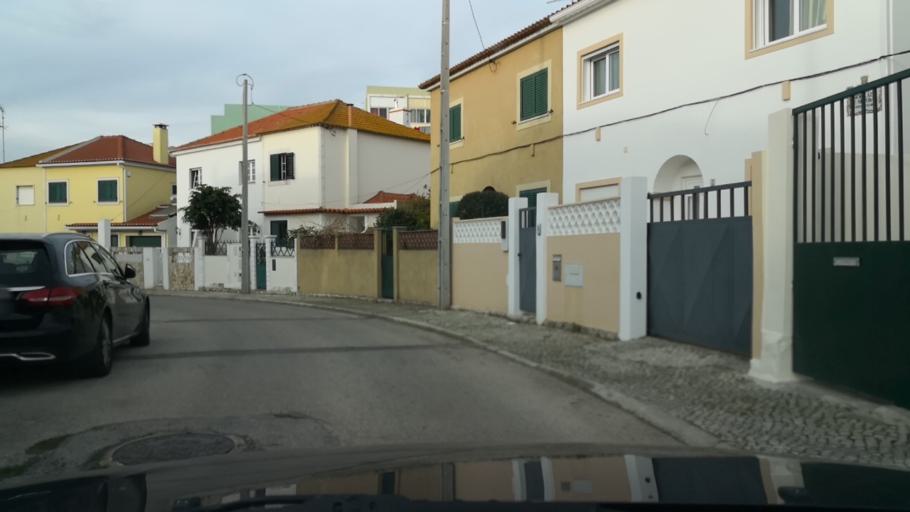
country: PT
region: Setubal
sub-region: Setubal
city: Setubal
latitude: 38.5243
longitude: -8.8758
